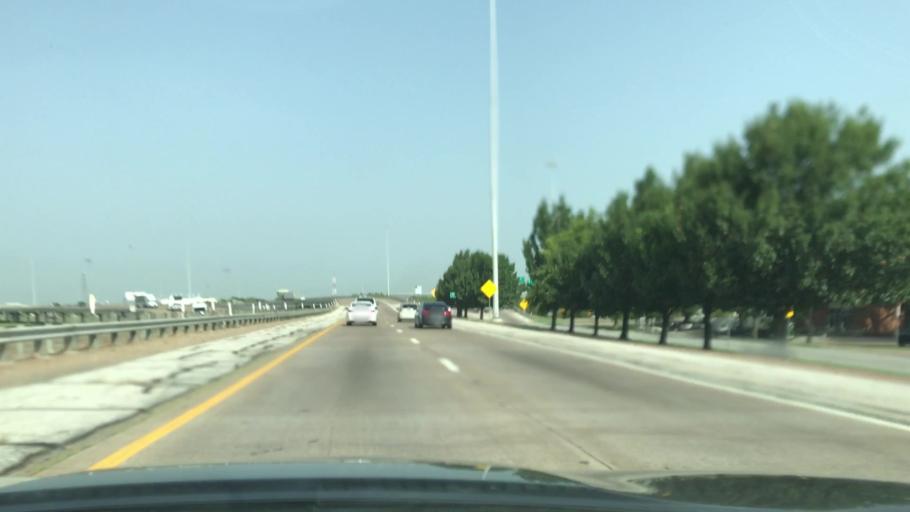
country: US
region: Texas
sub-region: Dallas County
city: Mesquite
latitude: 32.7988
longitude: -96.6726
